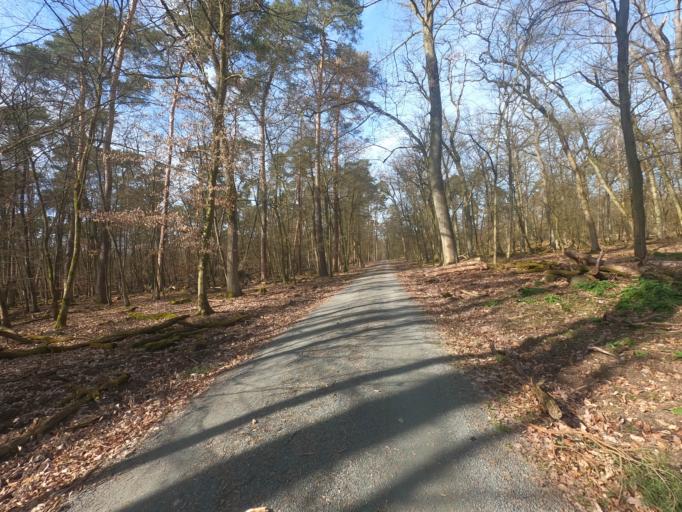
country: DE
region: Hesse
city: Raunheim
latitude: 49.9942
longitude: 8.4980
